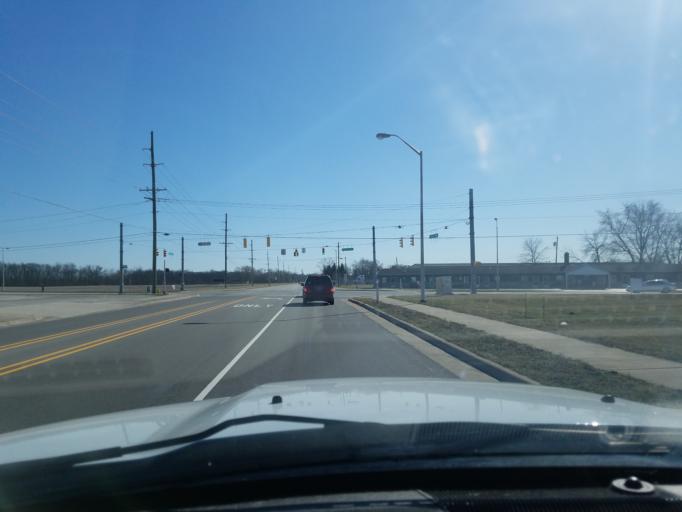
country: US
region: Indiana
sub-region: Shelby County
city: Shelbyville
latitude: 39.5167
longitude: -85.7426
